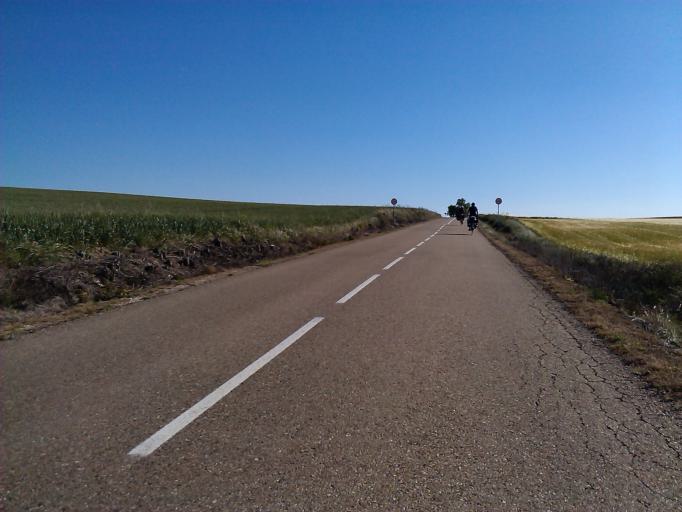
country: ES
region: Castille and Leon
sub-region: Provincia de Burgos
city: Itero del Castillo
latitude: 42.2929
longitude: -4.2237
